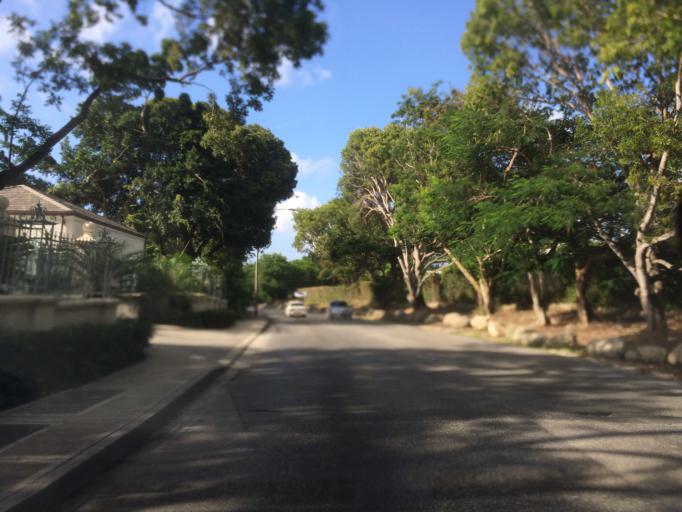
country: BB
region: Saint James
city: Holetown
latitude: 13.1749
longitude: -59.6359
